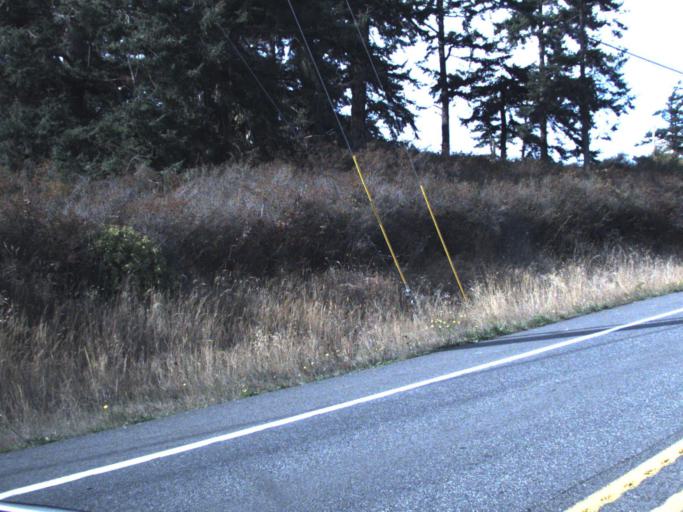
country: US
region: Washington
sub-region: Island County
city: Coupeville
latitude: 48.2427
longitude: -122.7141
